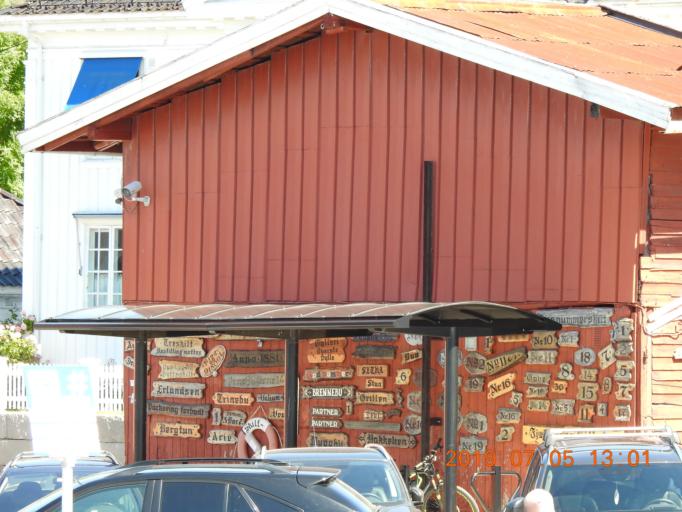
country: NO
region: Akershus
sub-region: Frogn
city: Drobak
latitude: 59.6609
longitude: 10.6274
